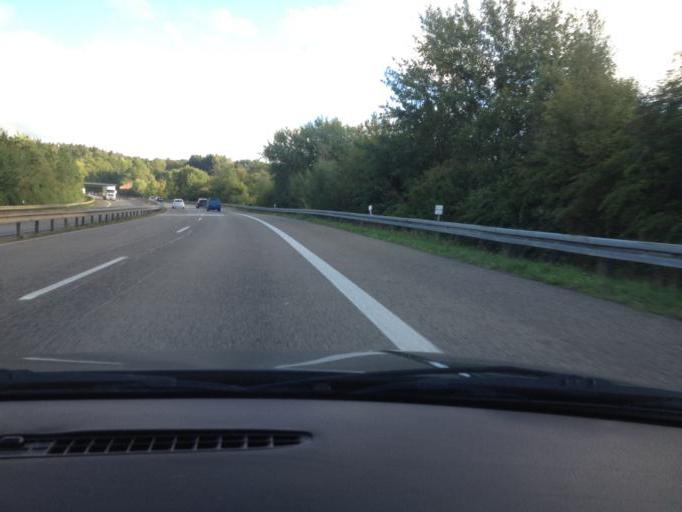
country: DE
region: Saarland
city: Eppelborn
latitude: 49.3983
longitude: 7.0082
